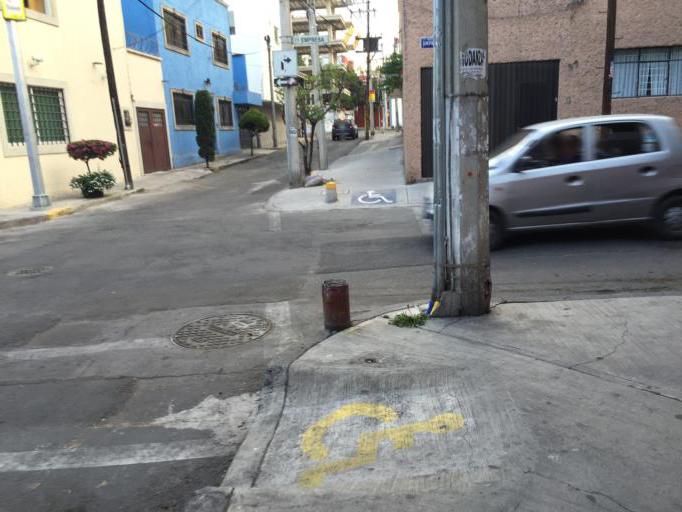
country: MX
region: Mexico City
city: Colonia del Valle
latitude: 19.3757
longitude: -99.1844
